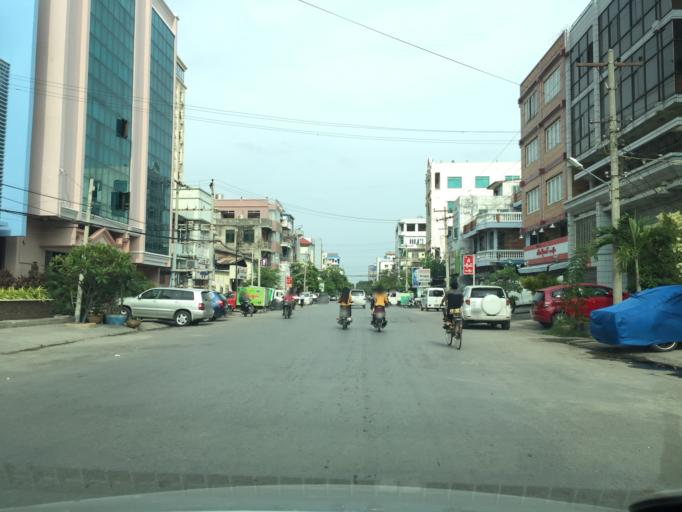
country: MM
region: Mandalay
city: Mandalay
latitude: 21.9741
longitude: 96.0818
